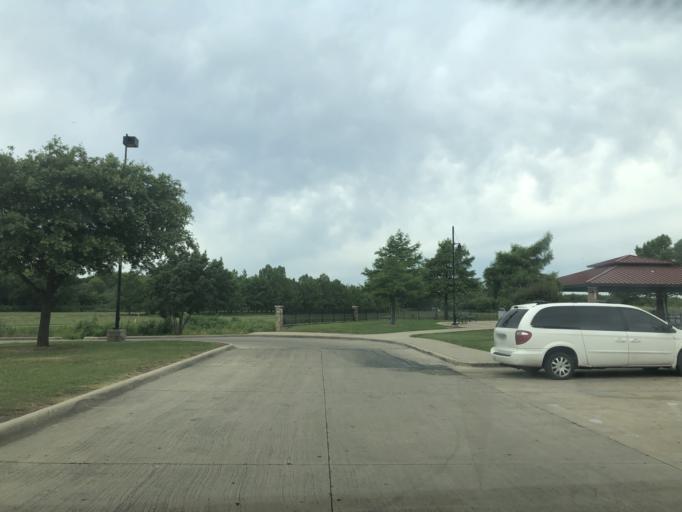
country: US
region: Texas
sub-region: Dallas County
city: Irving
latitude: 32.7868
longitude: -96.9792
